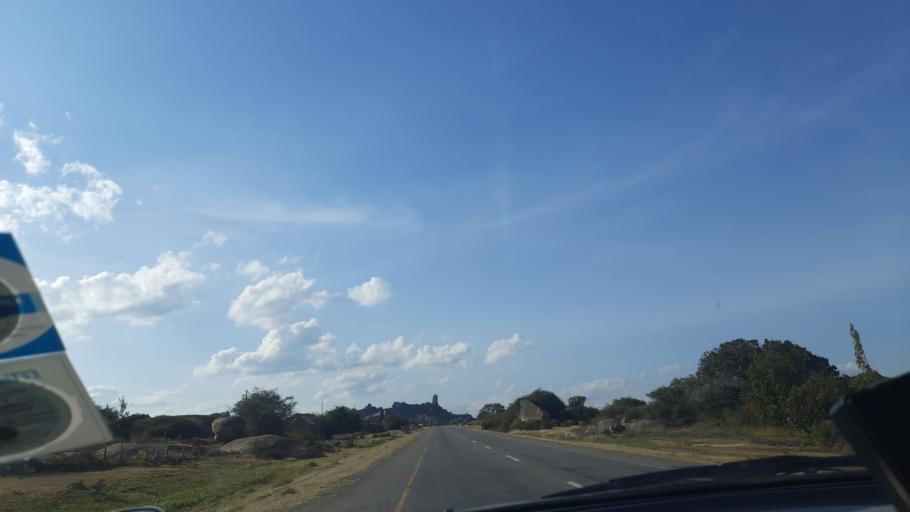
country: TZ
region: Singida
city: Puma
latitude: -4.9841
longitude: 34.7560
